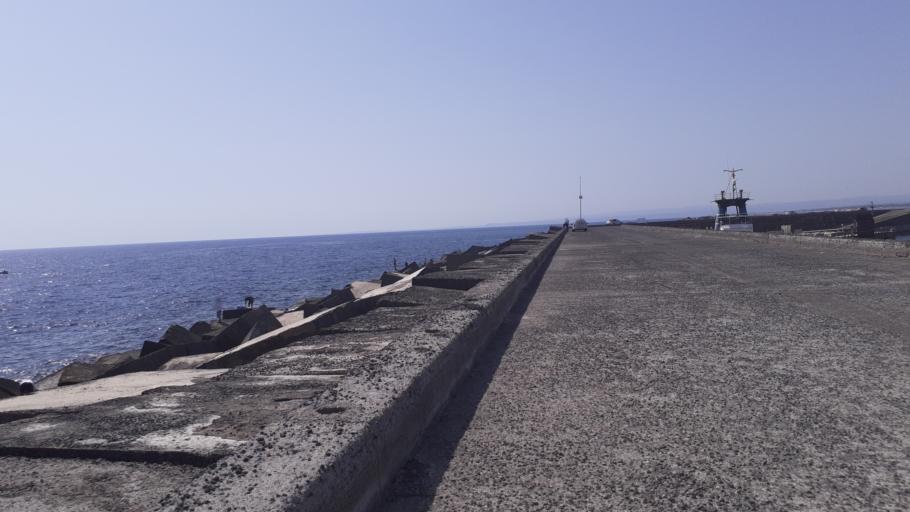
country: IT
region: Sicily
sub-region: Catania
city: Catania
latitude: 37.4895
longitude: 15.1001
